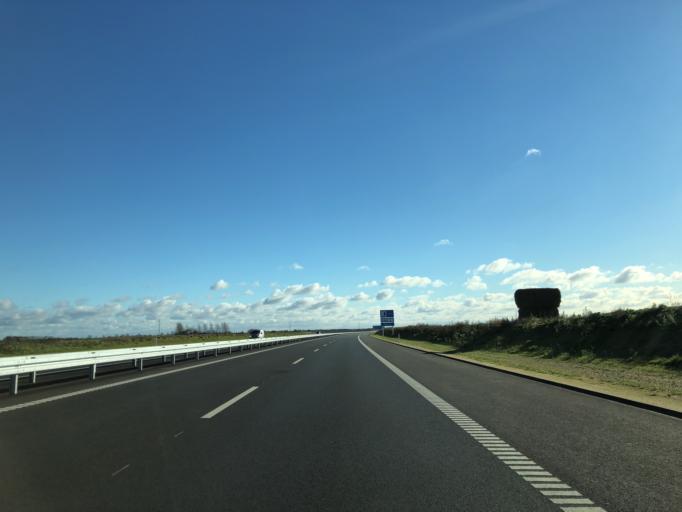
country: DK
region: Central Jutland
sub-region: Holstebro Kommune
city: Holstebro
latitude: 56.3741
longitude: 8.7068
